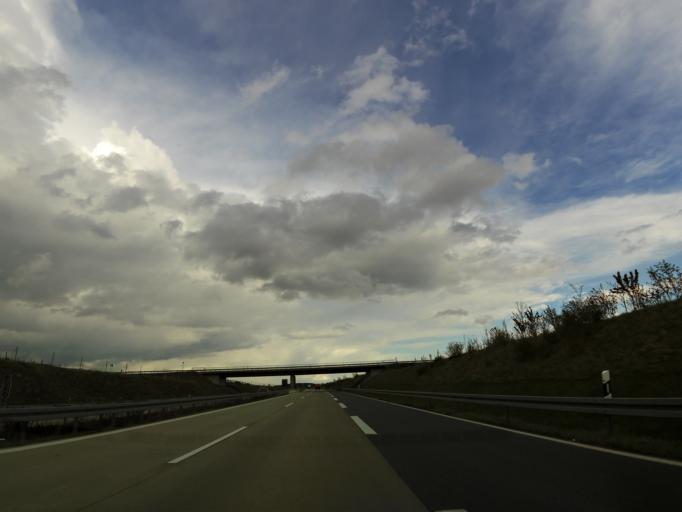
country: DE
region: Saxony-Anhalt
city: Timmenrode
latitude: 51.8046
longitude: 11.0008
